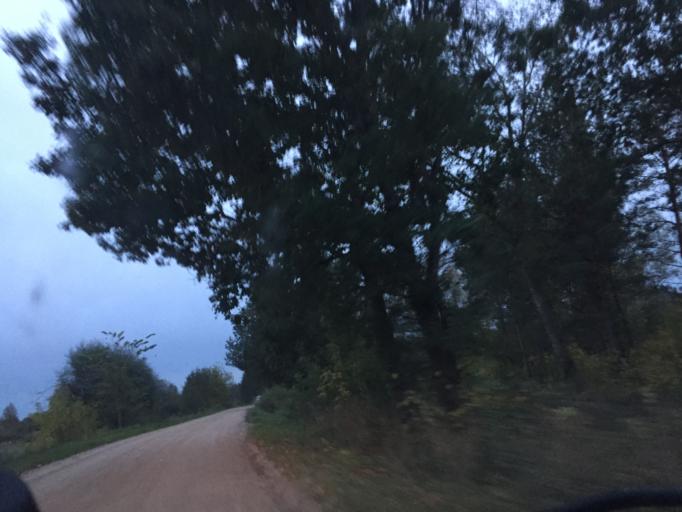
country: LV
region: Adazi
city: Adazi
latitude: 57.0806
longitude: 24.3694
